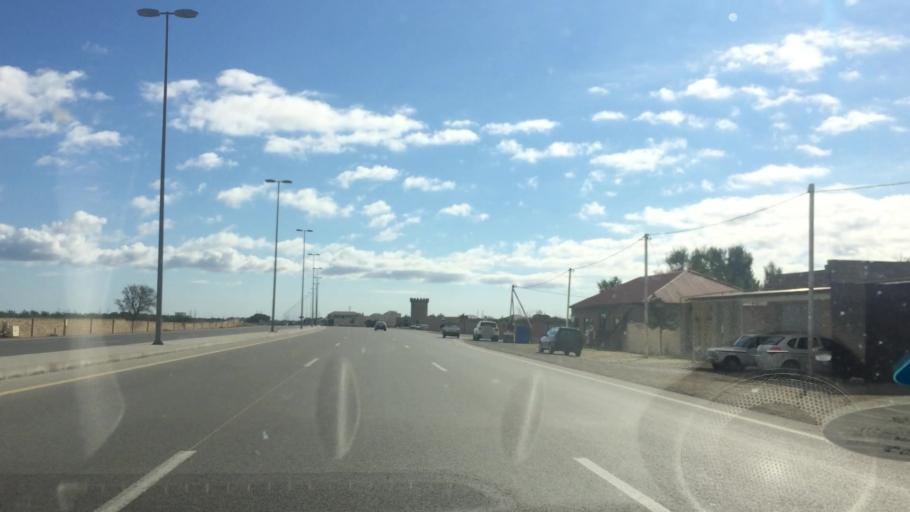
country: AZ
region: Baki
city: Qala
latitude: 40.4487
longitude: 50.1627
